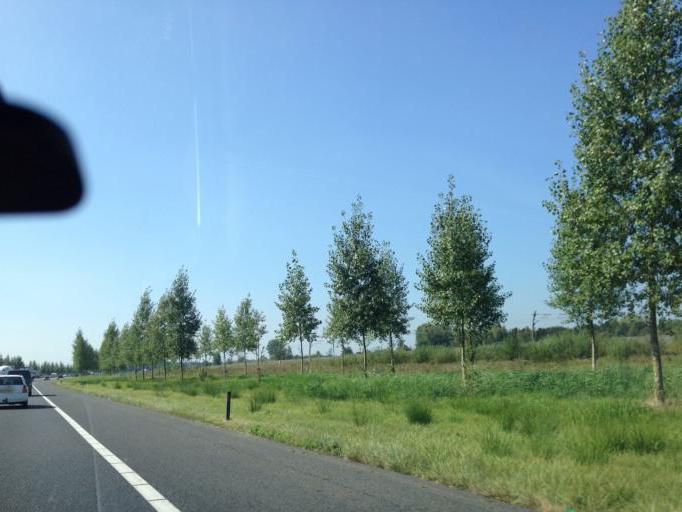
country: NL
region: Gelderland
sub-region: Gemeente Zaltbommel
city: Zaltbommel
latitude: 51.8534
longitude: 5.2159
